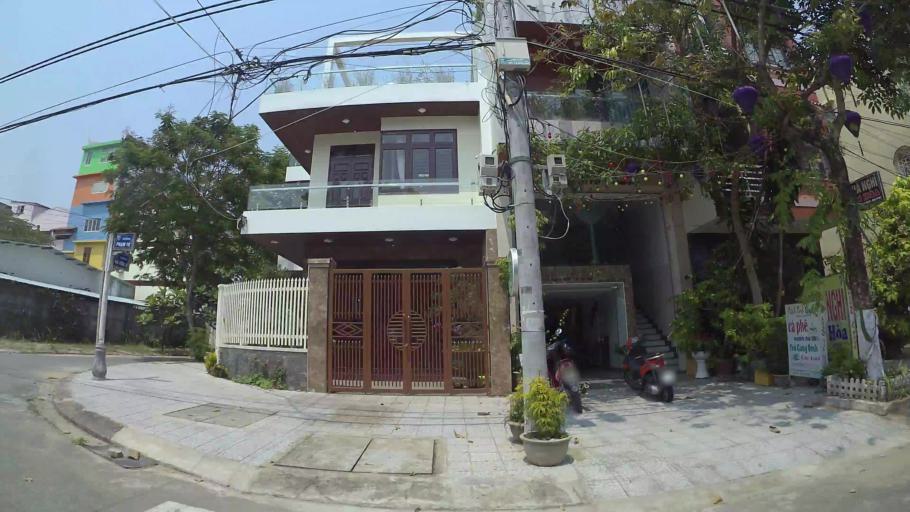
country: VN
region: Da Nang
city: Cam Le
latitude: 16.0179
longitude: 108.2103
